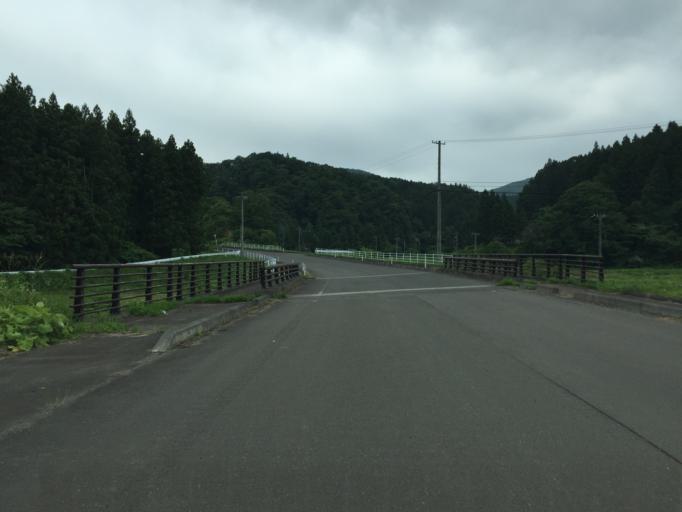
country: JP
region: Miyagi
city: Marumori
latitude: 37.8207
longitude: 140.7296
